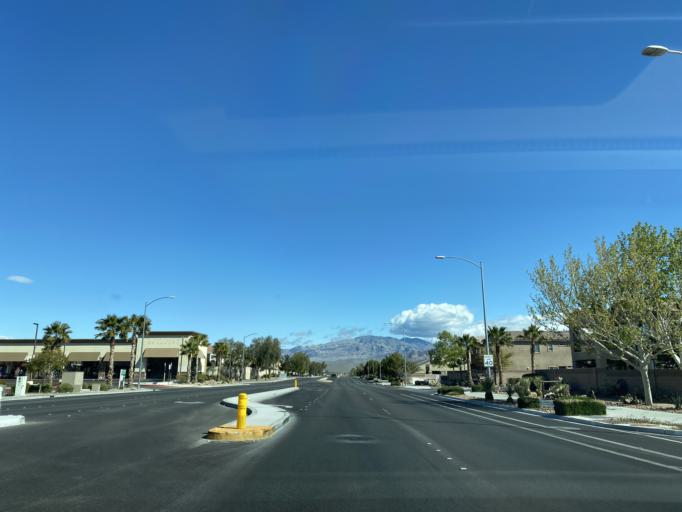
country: US
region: Nevada
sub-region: Clark County
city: Las Vegas
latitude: 36.3072
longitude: -115.2786
